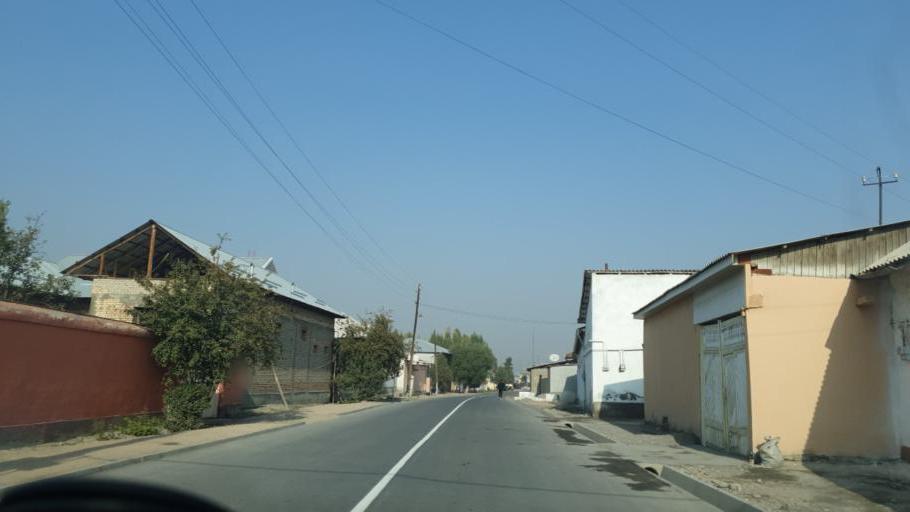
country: UZ
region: Fergana
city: Qo`qon
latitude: 40.5861
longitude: 70.9063
